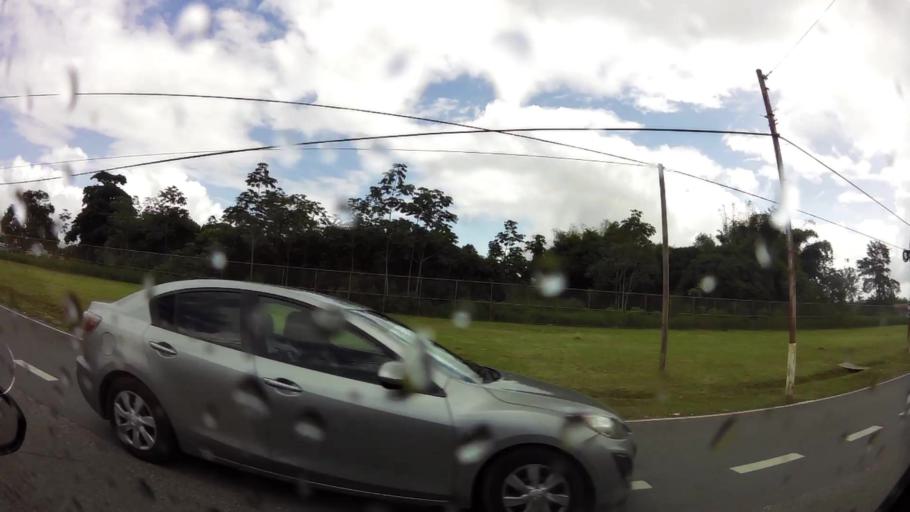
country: TT
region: Tunapuna/Piarco
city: Arouca
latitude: 10.6173
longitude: -61.3434
